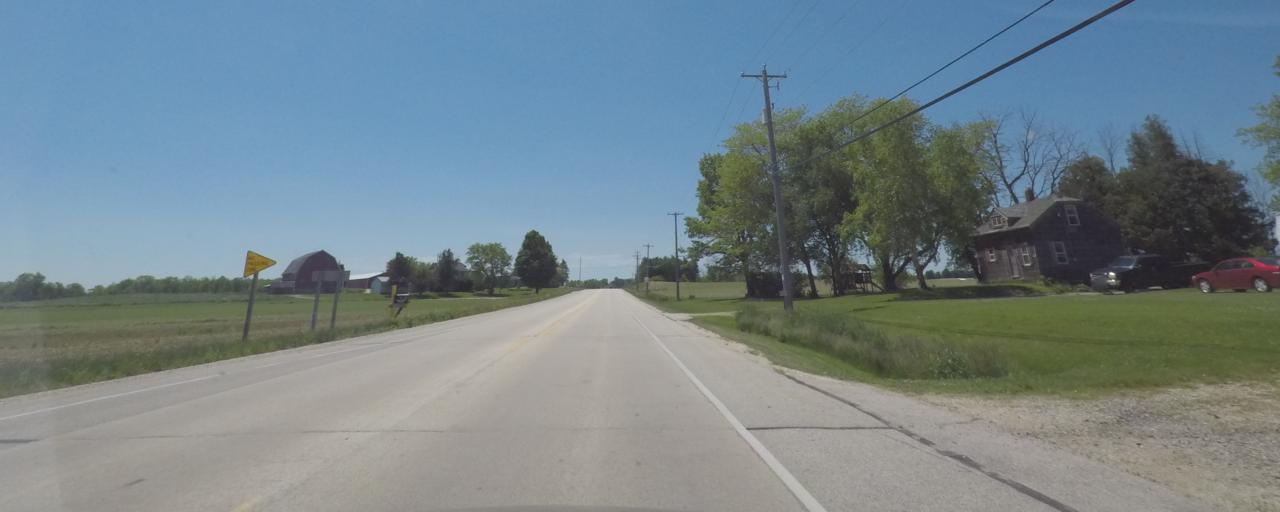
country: US
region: Wisconsin
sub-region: Washington County
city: West Bend
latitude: 43.4682
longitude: -88.1497
